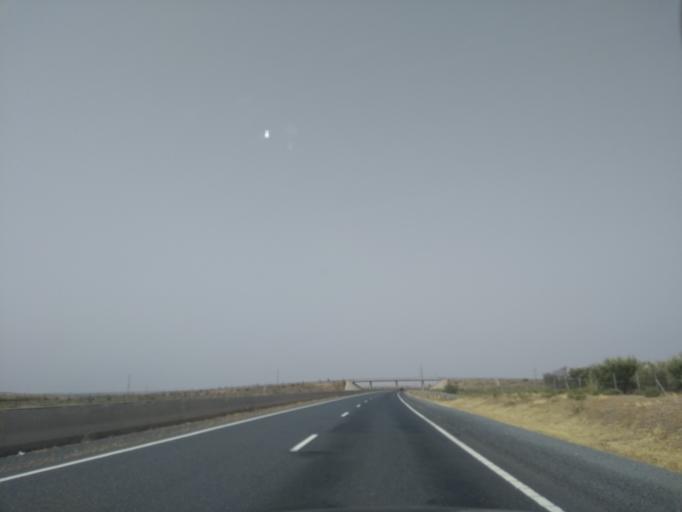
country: MA
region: Marrakech-Tensift-Al Haouz
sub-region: Marrakech
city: Marrakesh
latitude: 31.7610
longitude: -8.1829
